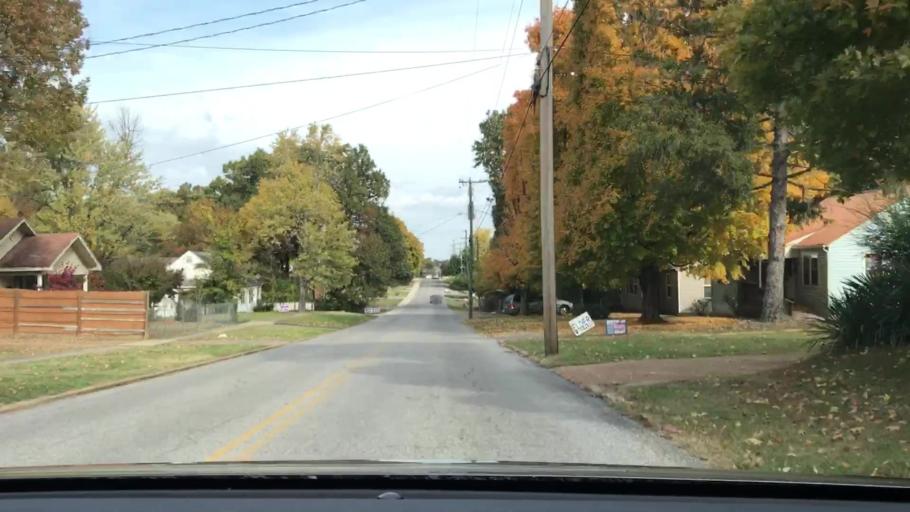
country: US
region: Kentucky
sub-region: Graves County
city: Mayfield
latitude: 36.7440
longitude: -88.6495
